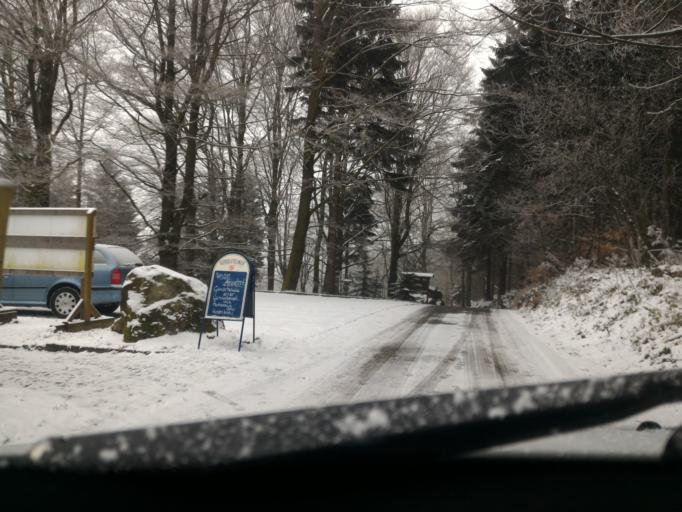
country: DE
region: Saxony
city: Kurort Jonsdorf
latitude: 50.8499
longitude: 14.6528
